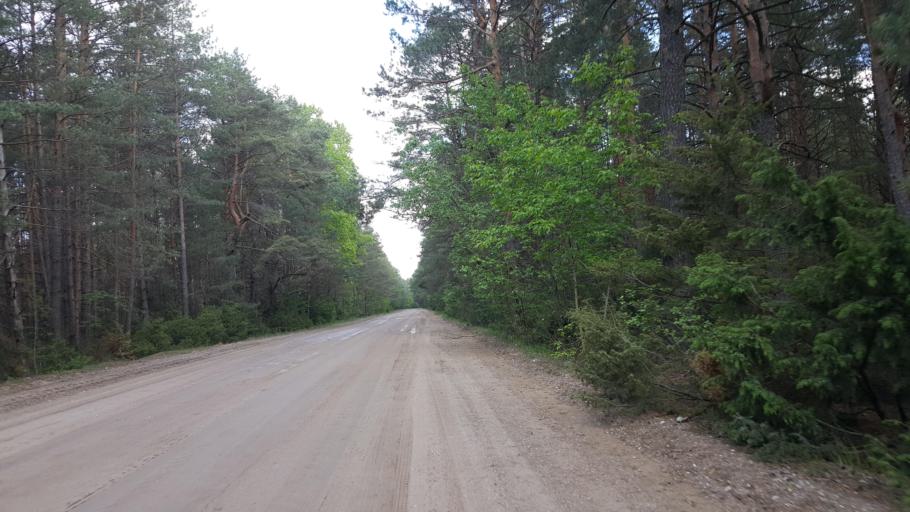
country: BY
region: Brest
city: Kamyanyets
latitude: 52.4309
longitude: 23.9724
